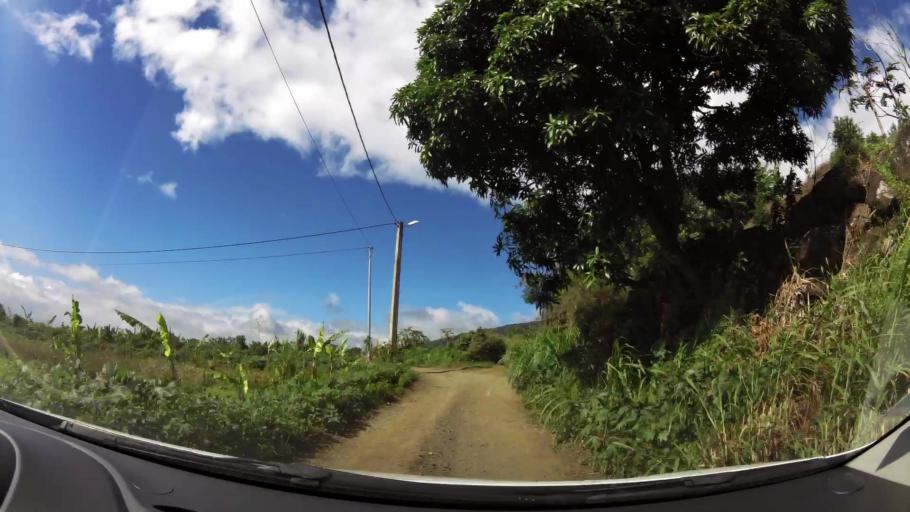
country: RE
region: Reunion
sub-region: Reunion
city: Sainte-Marie
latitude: -20.9296
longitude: 55.5002
